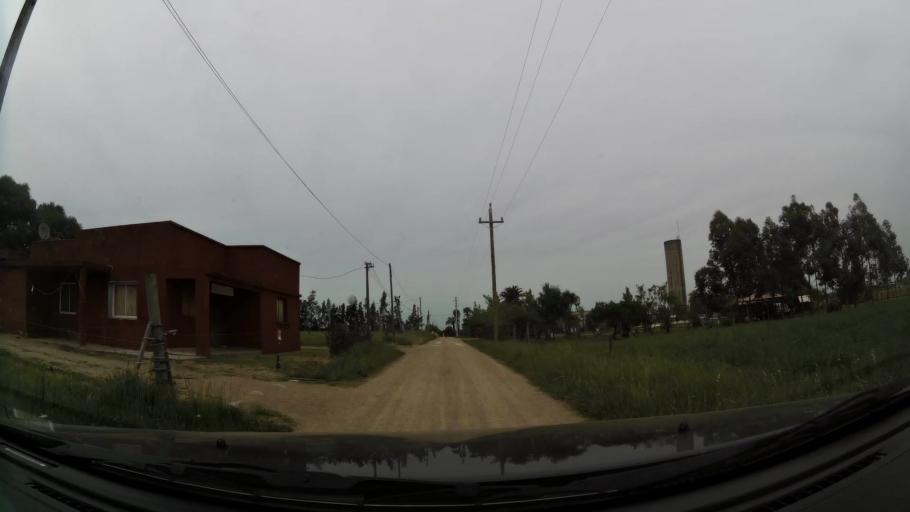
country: UY
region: Canelones
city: La Paz
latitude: -34.7444
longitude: -56.2362
